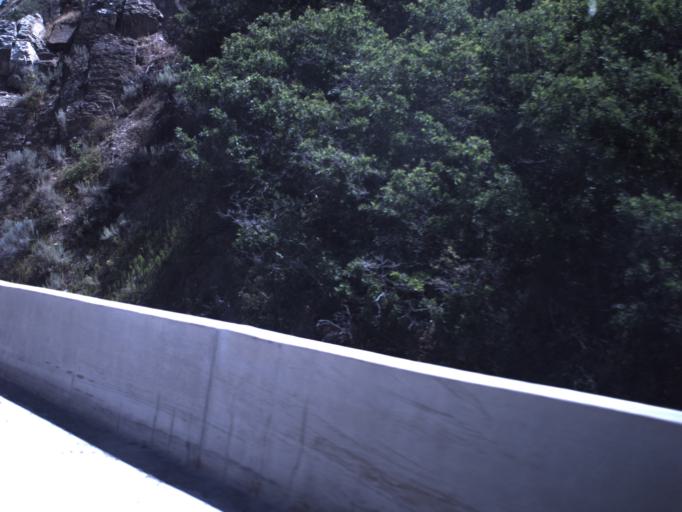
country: US
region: Utah
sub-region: Morgan County
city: Morgan
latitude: 41.0619
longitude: -111.5705
